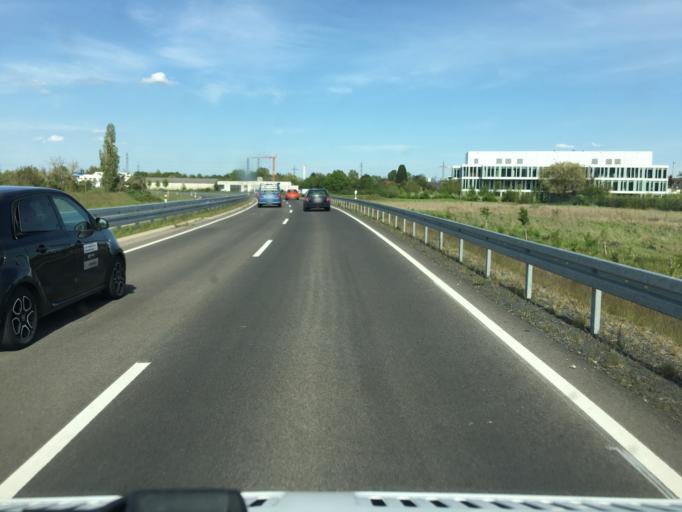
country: DE
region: North Rhine-Westphalia
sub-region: Regierungsbezirk Koln
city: Hurth
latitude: 50.8749
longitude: 6.8999
